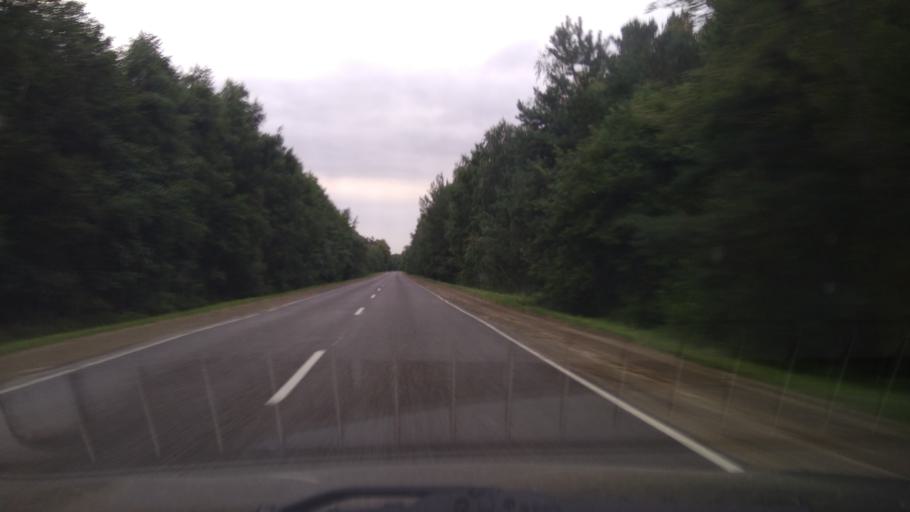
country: BY
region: Brest
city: Byaroza
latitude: 52.4087
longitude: 24.9958
